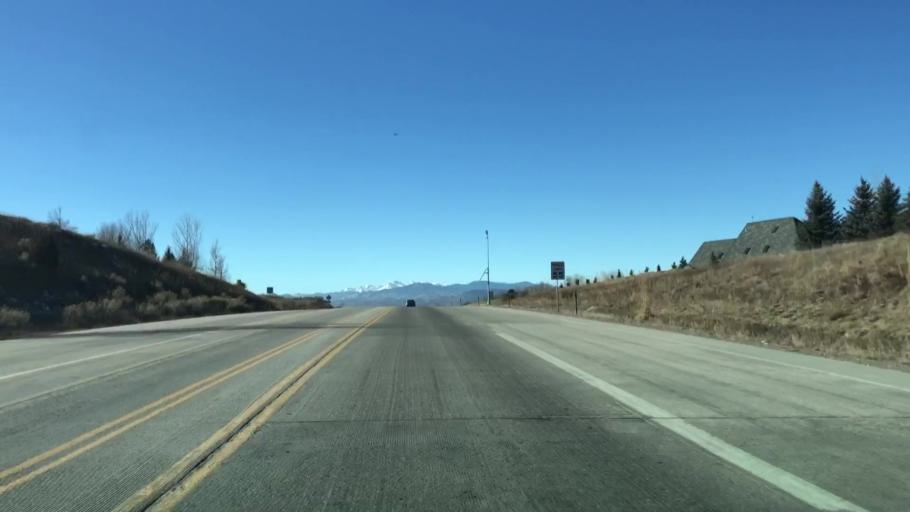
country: US
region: Colorado
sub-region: Weld County
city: Windsor
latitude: 40.4795
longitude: -104.9647
